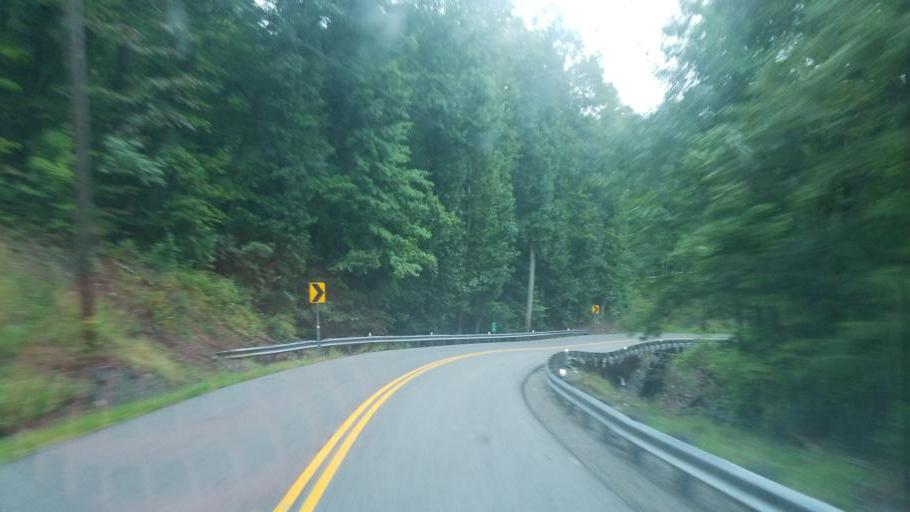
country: US
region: Kentucky
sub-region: Fleming County
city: Flemingsburg
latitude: 38.4049
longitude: -83.5796
